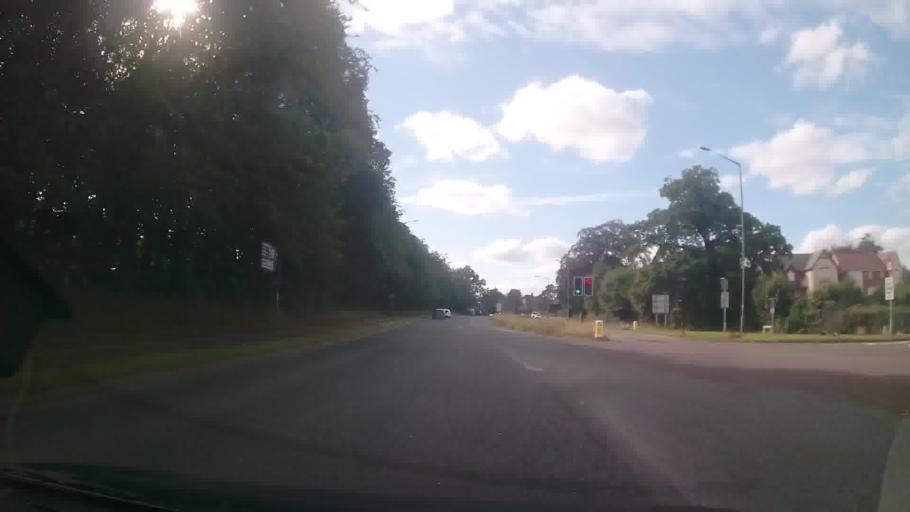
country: GB
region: England
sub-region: Shropshire
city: Bicton
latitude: 52.7136
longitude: -2.7891
